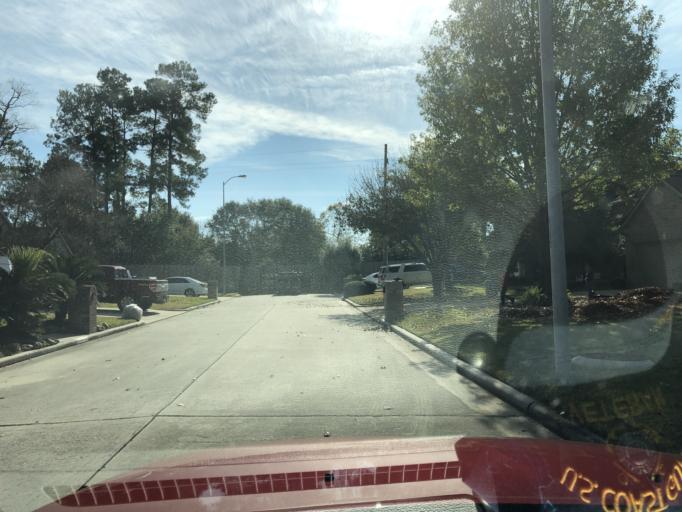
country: US
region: Texas
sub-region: Harris County
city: Tomball
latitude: 30.0258
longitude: -95.5562
